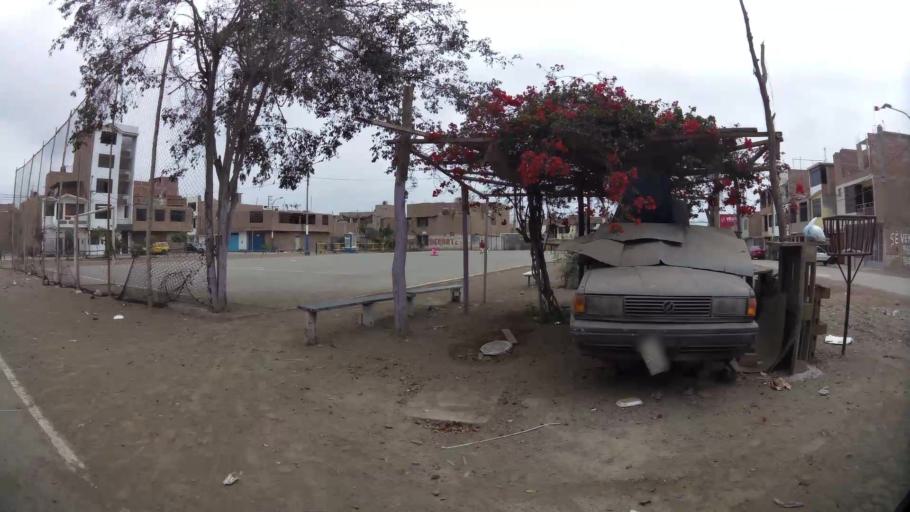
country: PE
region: Lima
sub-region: Lima
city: Independencia
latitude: -11.9675
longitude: -77.0948
